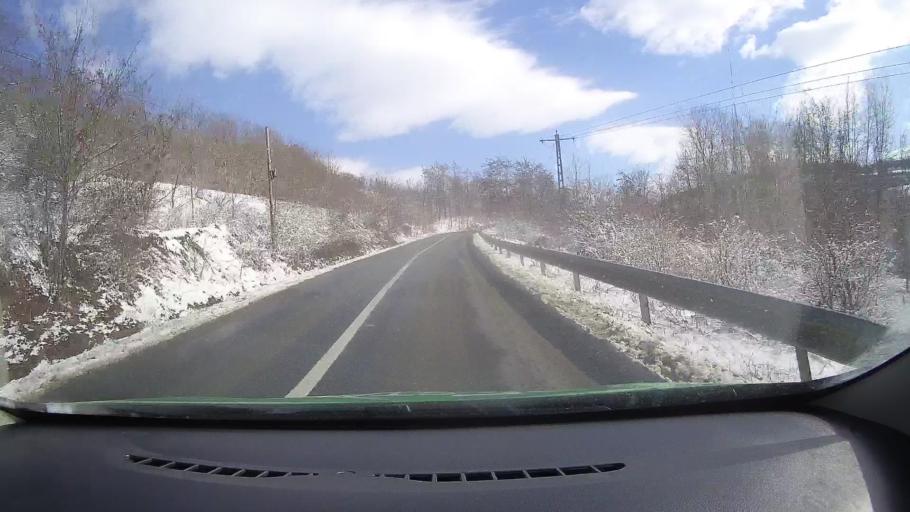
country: RO
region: Sibiu
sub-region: Comuna Barghis
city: Barghis
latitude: 45.9844
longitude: 24.5056
